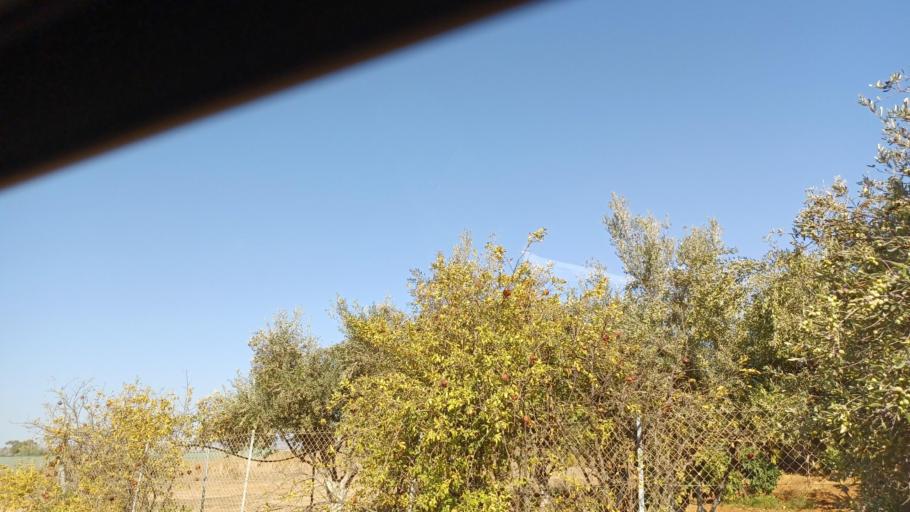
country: CY
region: Larnaka
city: Kolossi
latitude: 34.6690
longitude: 32.9499
